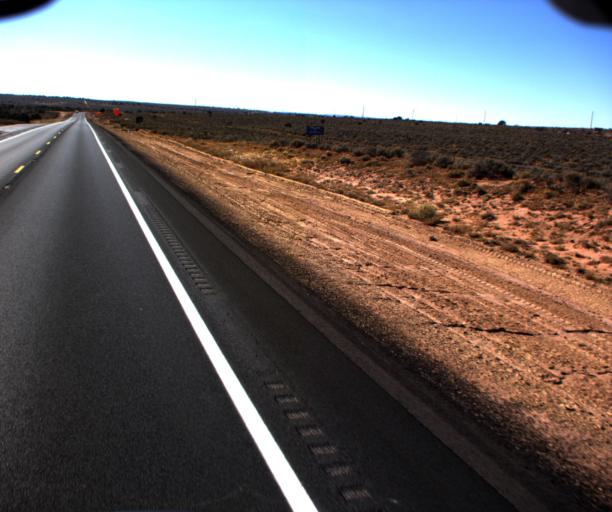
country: US
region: Arizona
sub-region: Apache County
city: Ganado
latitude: 35.7155
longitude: -109.4842
